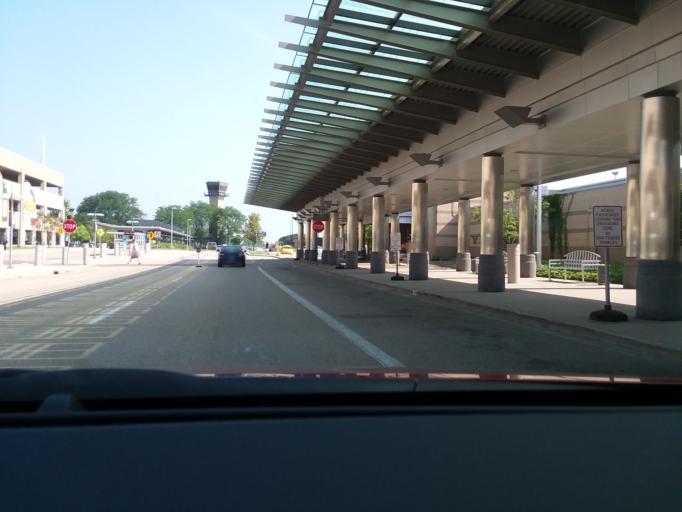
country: US
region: Wisconsin
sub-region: Dane County
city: Maple Bluff
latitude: 43.1367
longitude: -89.3464
